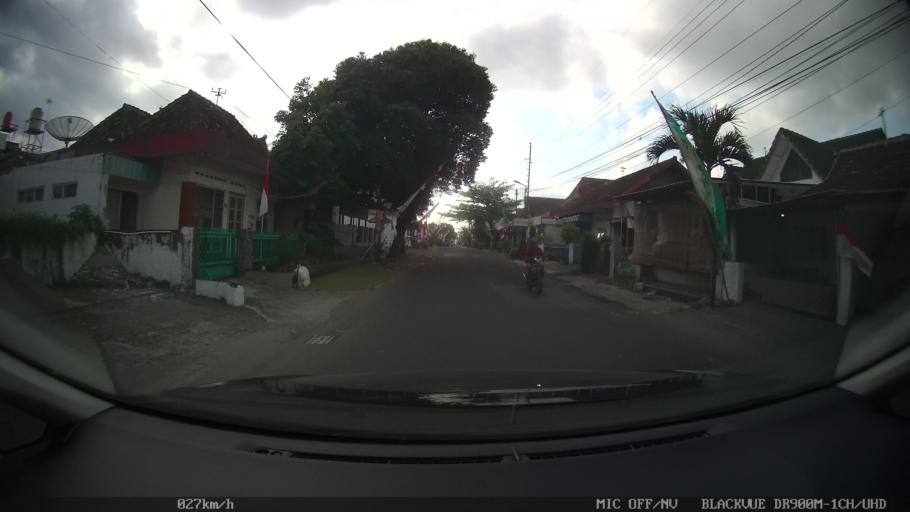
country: ID
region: Daerah Istimewa Yogyakarta
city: Kasihan
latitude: -7.8209
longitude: 110.3626
